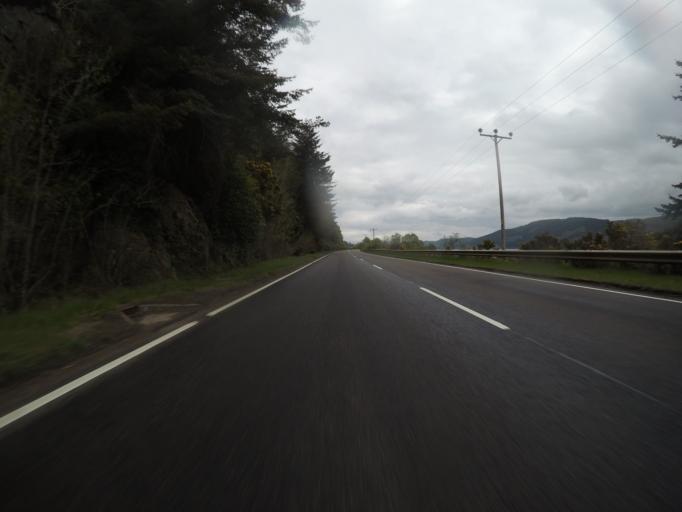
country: GB
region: Scotland
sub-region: Highland
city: Beauly
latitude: 57.2283
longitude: -4.5690
